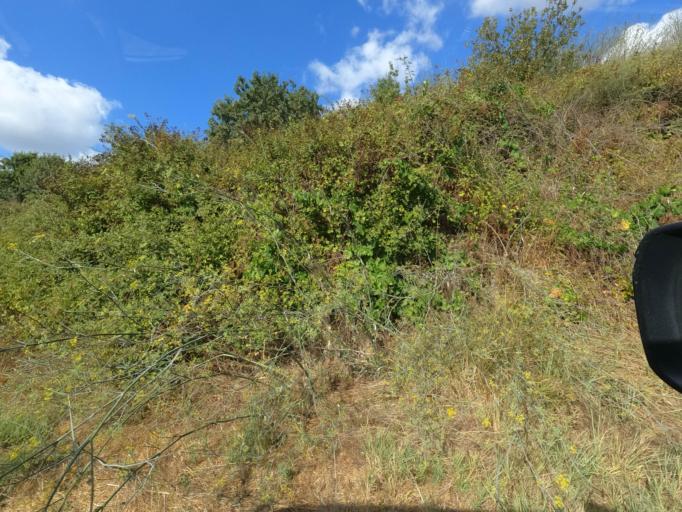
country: CY
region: Pafos
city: Mesogi
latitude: 34.8419
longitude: 32.5430
